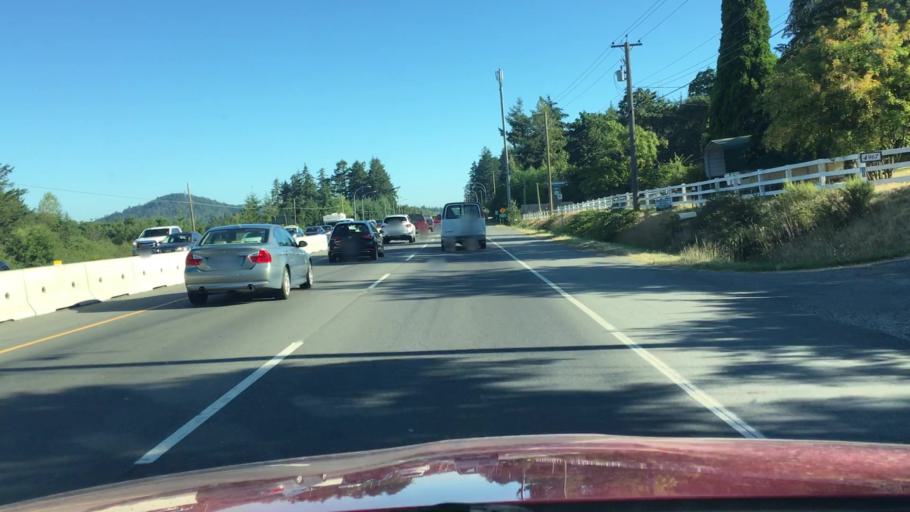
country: CA
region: British Columbia
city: Victoria
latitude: 48.5156
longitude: -123.3845
